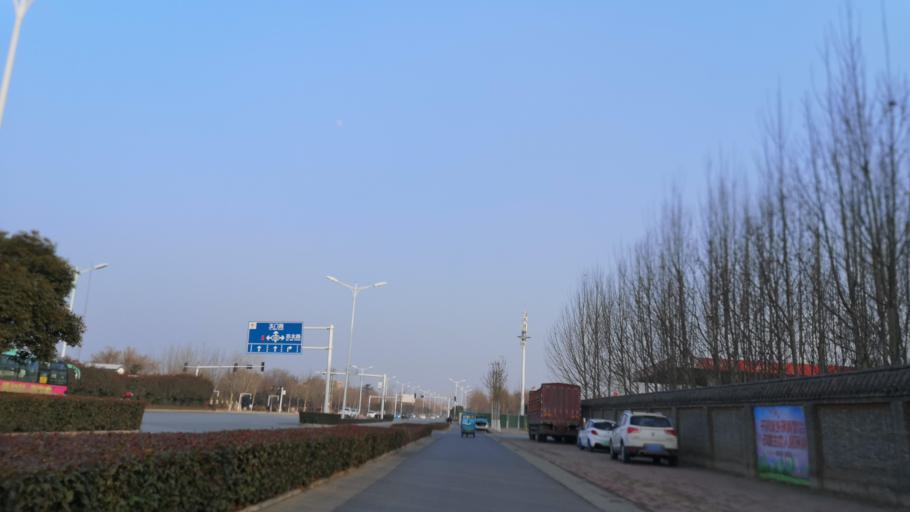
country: CN
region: Henan Sheng
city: Zhongyuanlu
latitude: 35.7905
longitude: 115.0615
